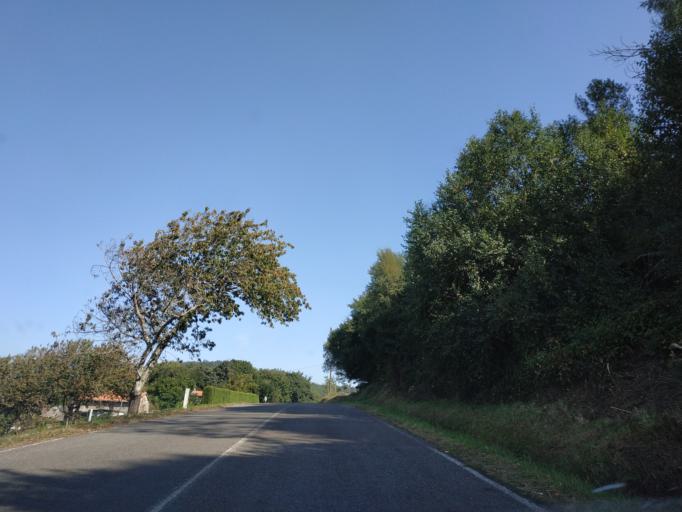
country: ES
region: Galicia
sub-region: Provincia da Coruna
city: Laracha
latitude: 43.2280
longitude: -8.5529
